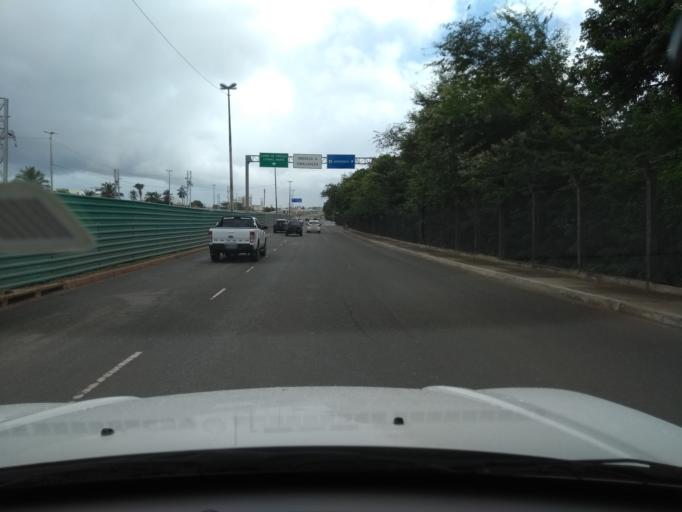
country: BR
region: Bahia
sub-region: Lauro De Freitas
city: Lauro de Freitas
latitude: -12.9144
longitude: -38.3461
